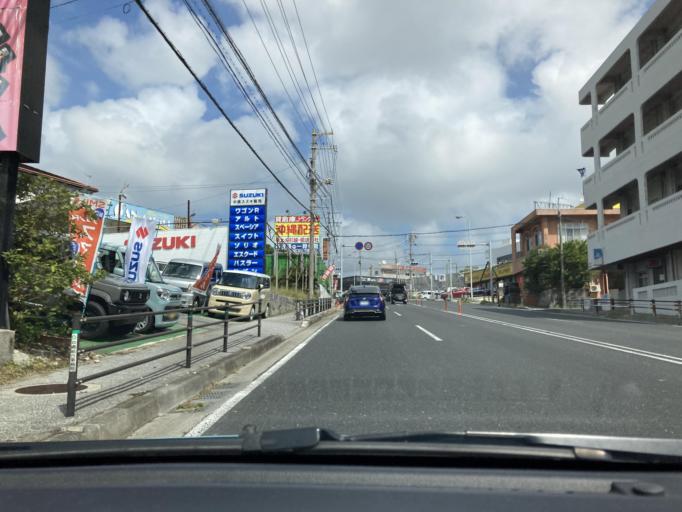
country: JP
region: Okinawa
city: Okinawa
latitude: 26.3300
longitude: 127.8223
